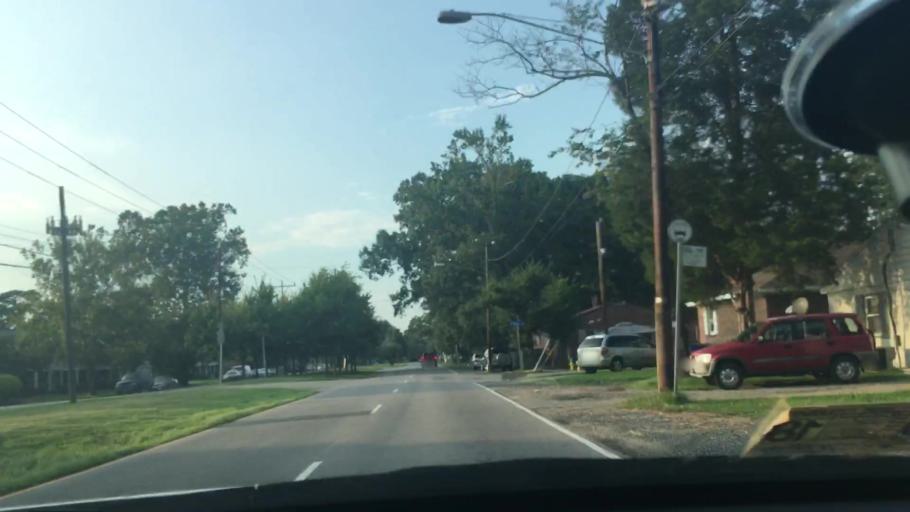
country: US
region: Virginia
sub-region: City of Norfolk
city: Norfolk
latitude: 36.9390
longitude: -76.2451
